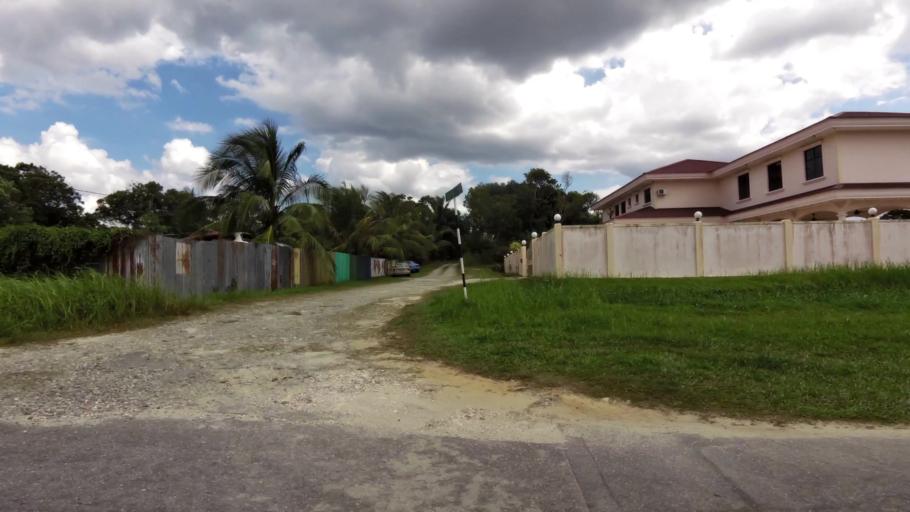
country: BN
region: Brunei and Muara
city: Bandar Seri Begawan
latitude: 4.9496
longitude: 114.9567
